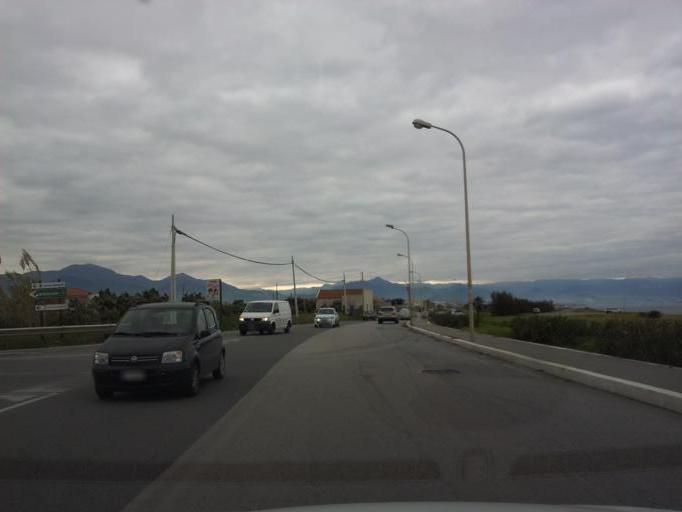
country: IT
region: Sicily
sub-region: Messina
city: Milazzo
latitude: 38.2062
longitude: 15.2275
